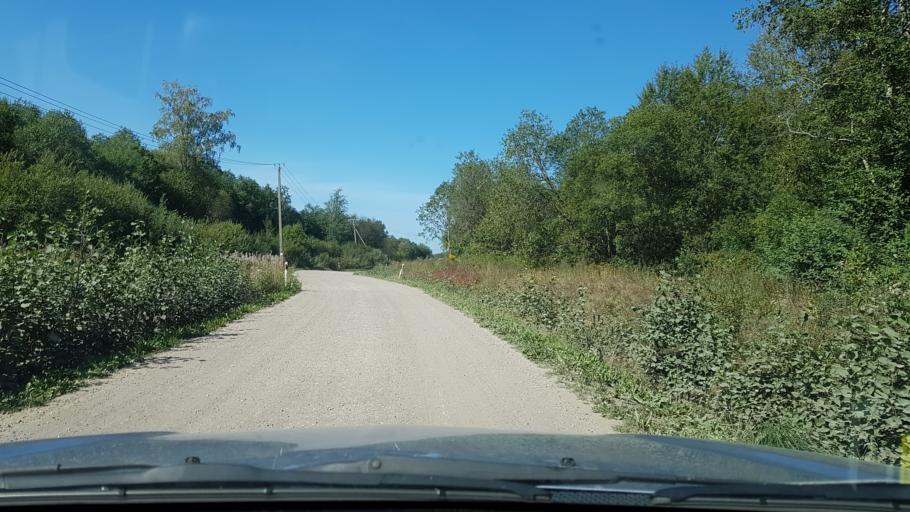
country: EE
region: Ida-Virumaa
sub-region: Sillamaee linn
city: Sillamae
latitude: 59.3766
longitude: 27.7769
